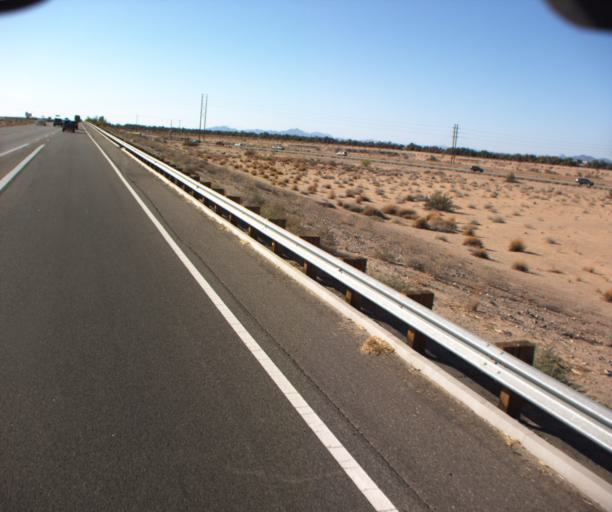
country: US
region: Arizona
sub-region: Yuma County
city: Fortuna Foothills
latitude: 32.6729
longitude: -114.4878
